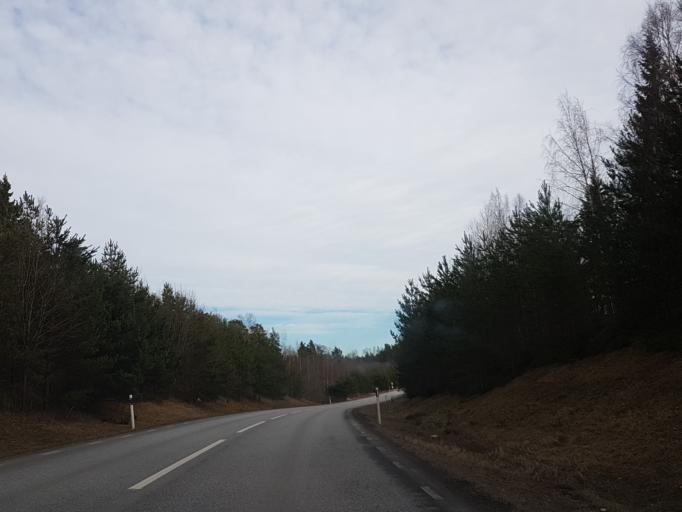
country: SE
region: Stockholm
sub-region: Norrtalje Kommun
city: Norrtalje
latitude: 59.6813
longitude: 18.8030
